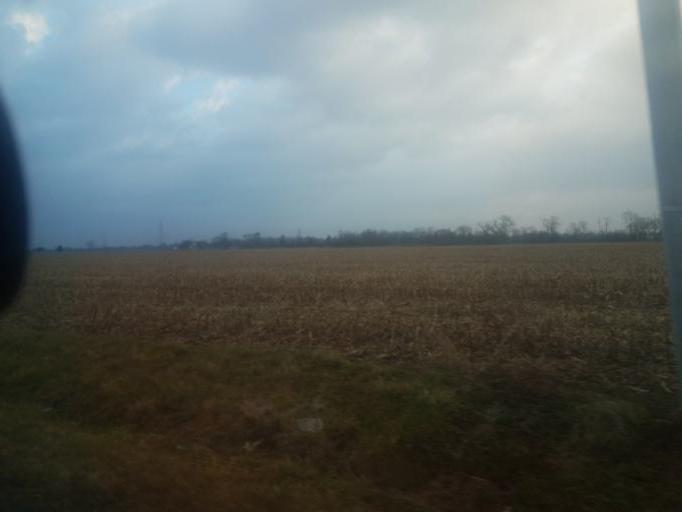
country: US
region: Ohio
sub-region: Marion County
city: Marion
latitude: 40.5971
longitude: -83.1688
